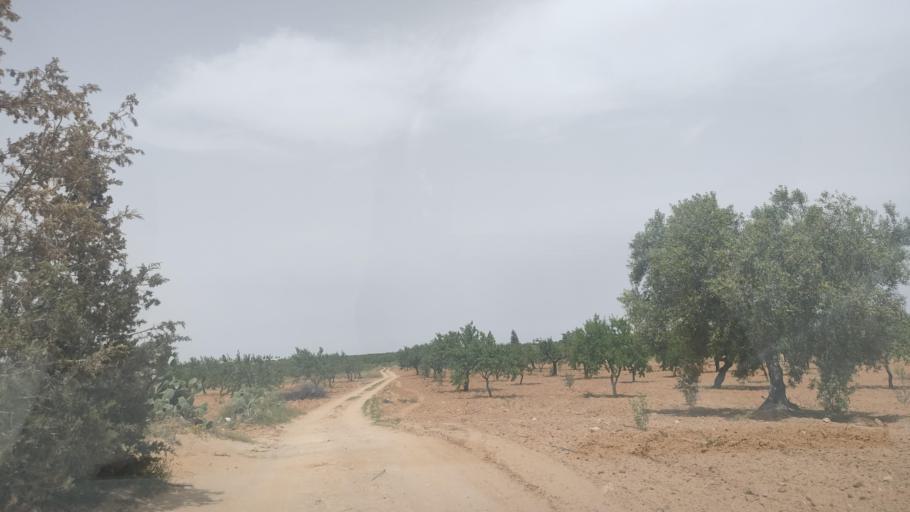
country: TN
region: Safaqis
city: Sfax
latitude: 34.8418
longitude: 10.5931
